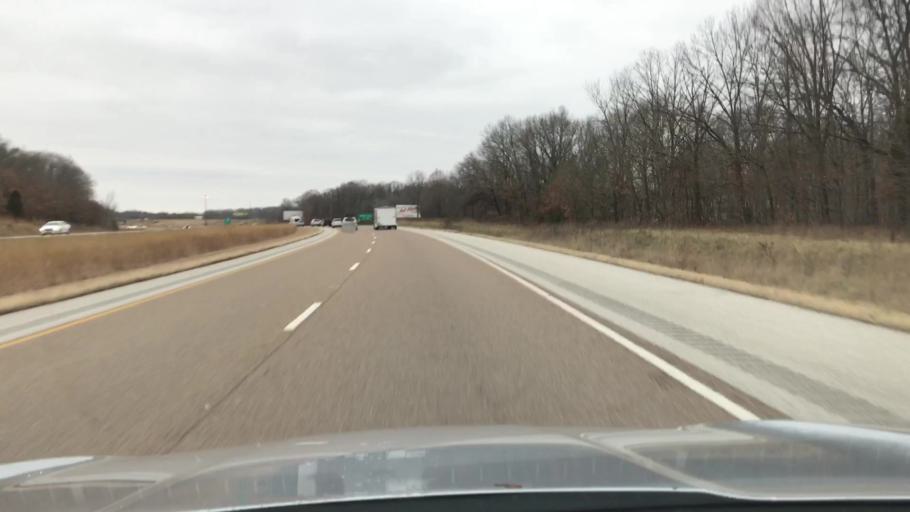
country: US
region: Illinois
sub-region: Macoupin County
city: Mount Olive
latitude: 39.0821
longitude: -89.7547
